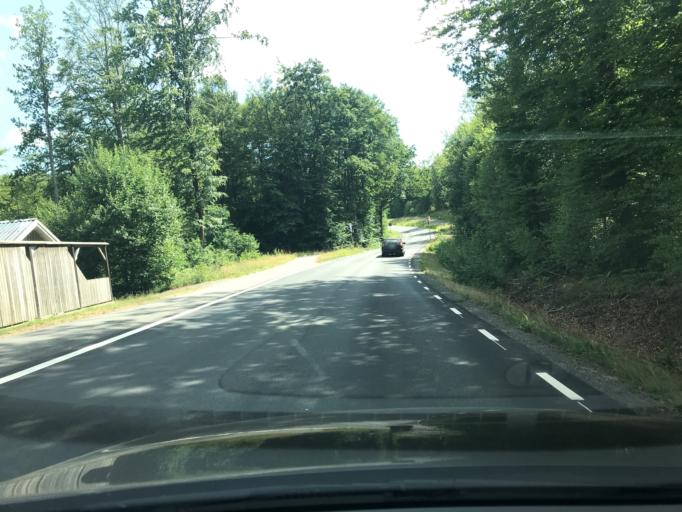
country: SE
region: Skane
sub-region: Hassleholms Kommun
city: Hastveda
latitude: 56.2804
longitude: 13.9142
